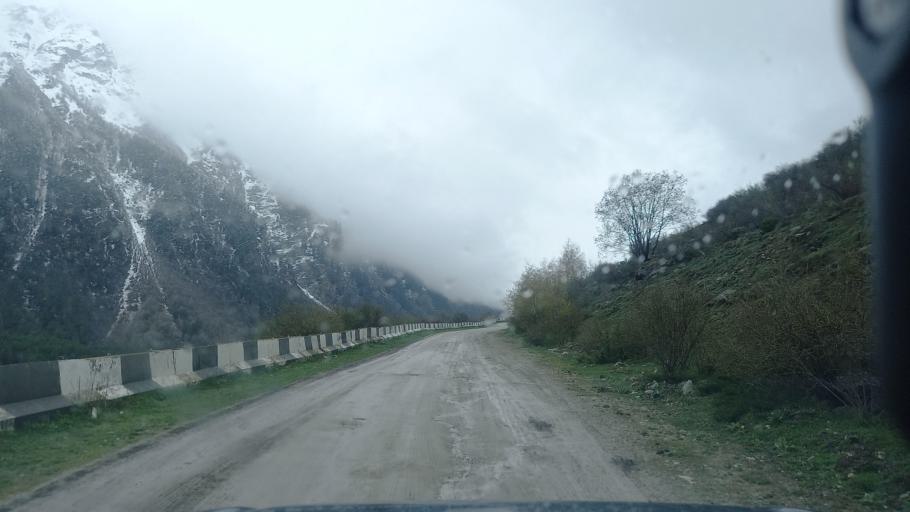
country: RU
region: Kabardino-Balkariya
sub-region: El'brusskiy Rayon
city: El'brus
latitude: 43.2263
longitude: 42.6643
